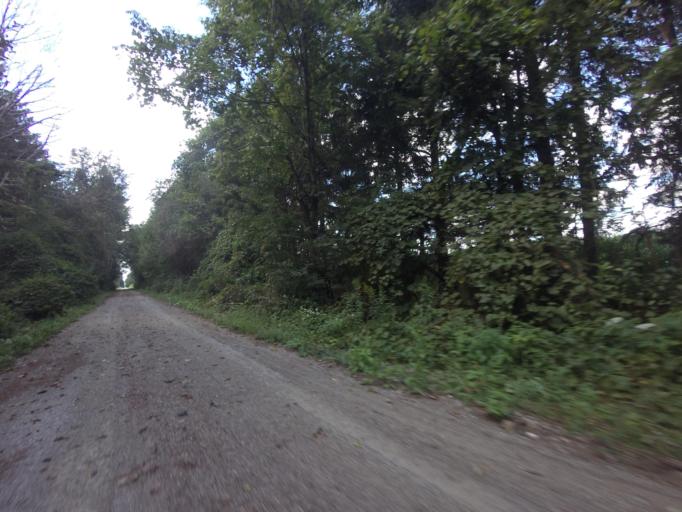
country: CA
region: Ontario
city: Huron East
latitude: 43.6580
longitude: -81.2457
